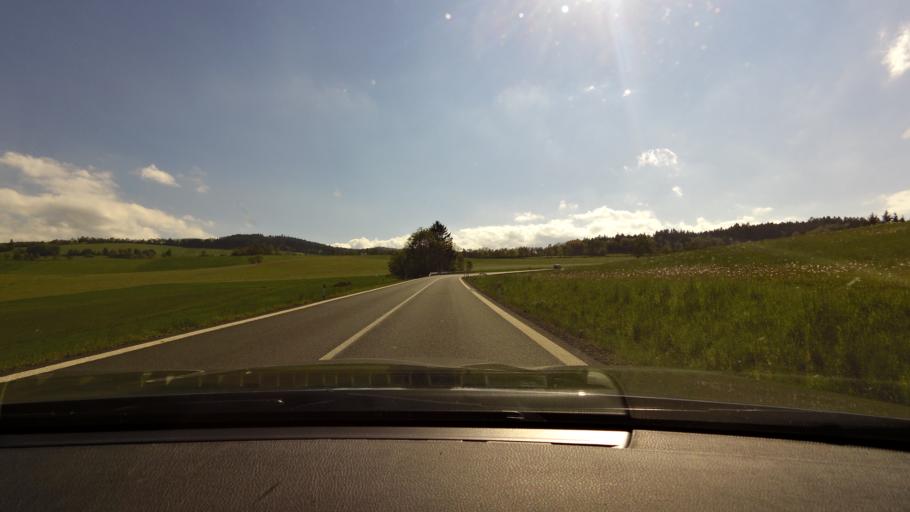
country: CZ
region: Plzensky
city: Strazov
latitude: 49.2815
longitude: 13.2979
